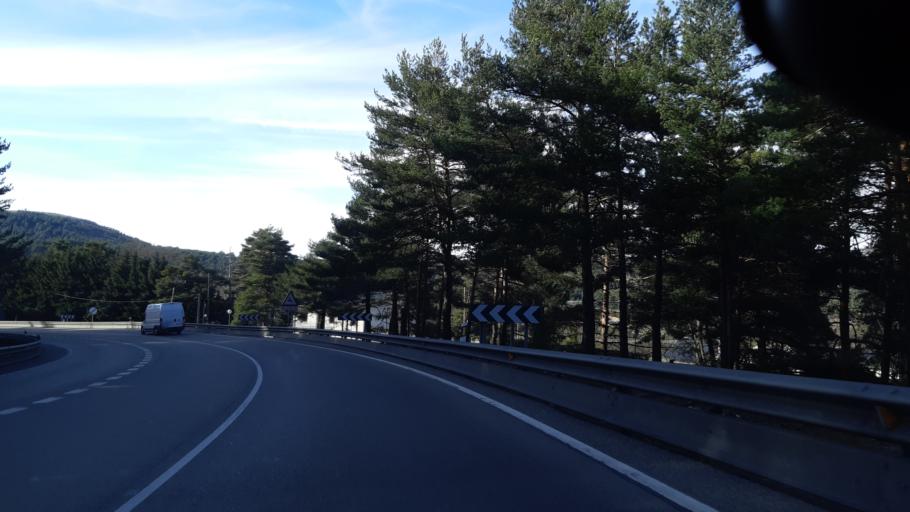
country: ES
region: Madrid
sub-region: Provincia de Madrid
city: Guadarrama
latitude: 40.7121
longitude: -4.1597
